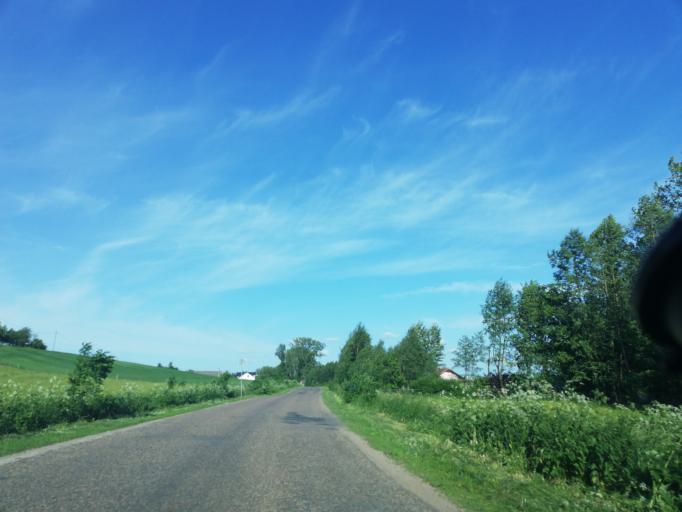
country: PL
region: Kujawsko-Pomorskie
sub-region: Powiat golubsko-dobrzynski
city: Golub-Dobrzyn
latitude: 53.0388
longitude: 19.0845
